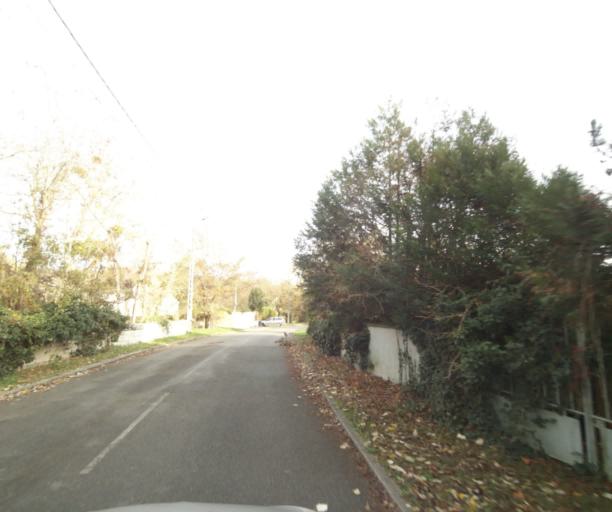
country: FR
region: Ile-de-France
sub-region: Departement des Yvelines
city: Maurecourt
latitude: 48.9838
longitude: 2.0787
